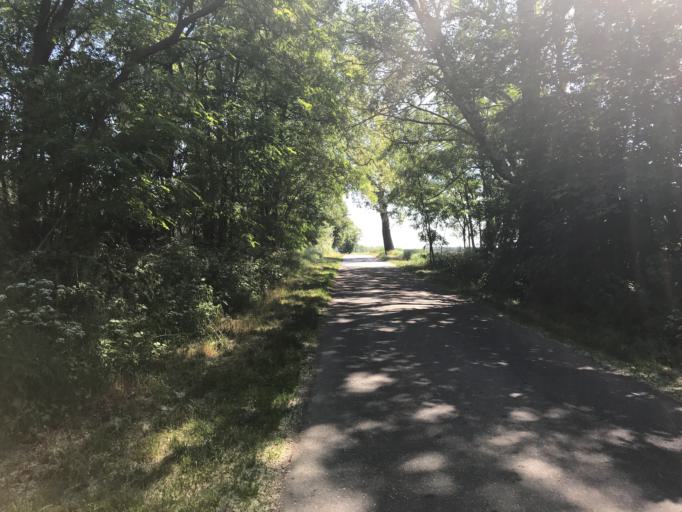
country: PL
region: West Pomeranian Voivodeship
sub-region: Powiat gryfinski
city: Mieszkowice
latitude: 52.7402
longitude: 14.4959
